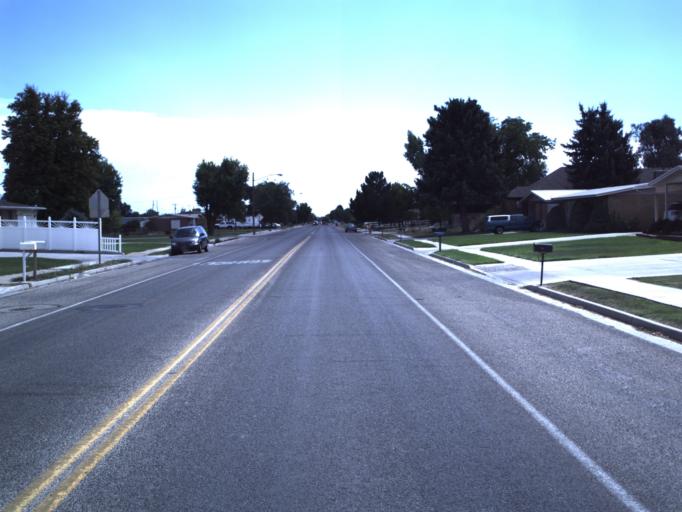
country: US
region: Utah
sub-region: Box Elder County
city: Garland
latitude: 41.7349
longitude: -112.1625
